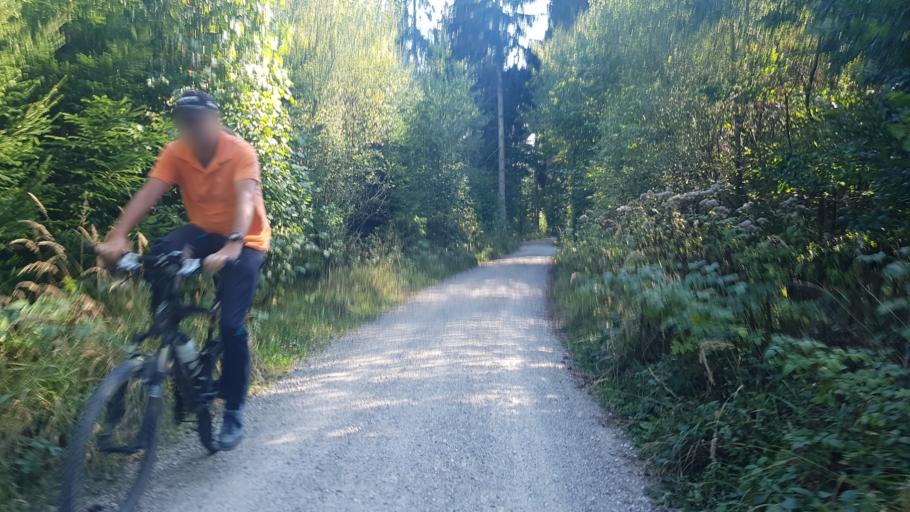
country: DE
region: Bavaria
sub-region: Upper Bavaria
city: Gilching
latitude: 48.0855
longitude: 11.3024
